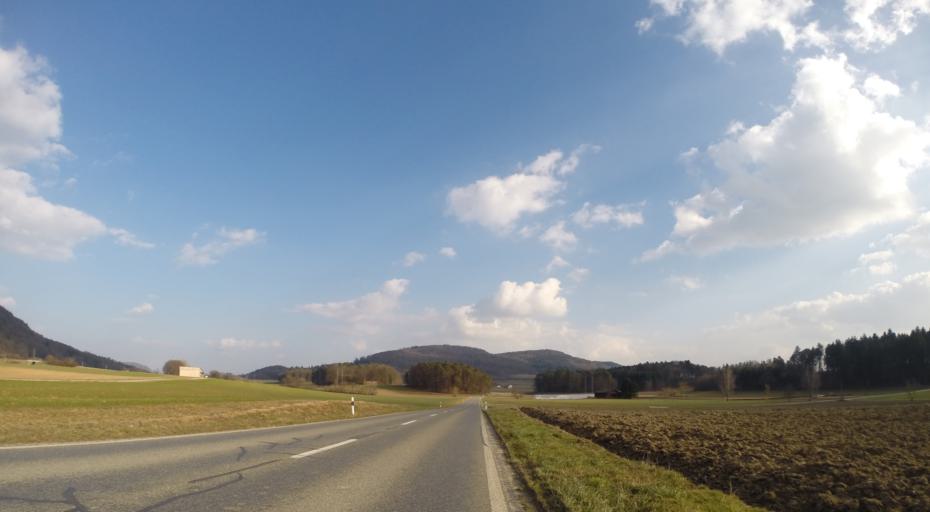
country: CH
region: Thurgau
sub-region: Frauenfeld District
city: Diessenhofen
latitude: 47.6630
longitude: 8.7769
